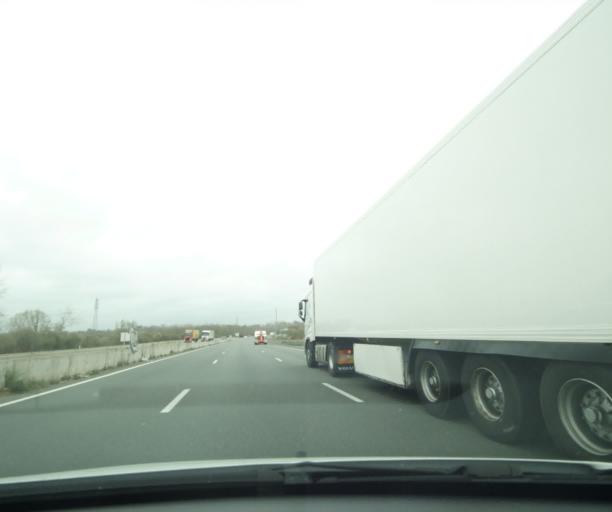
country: FR
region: Aquitaine
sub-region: Departement des Pyrenees-Atlantiques
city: Bayonne
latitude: 43.4674
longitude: -1.4795
